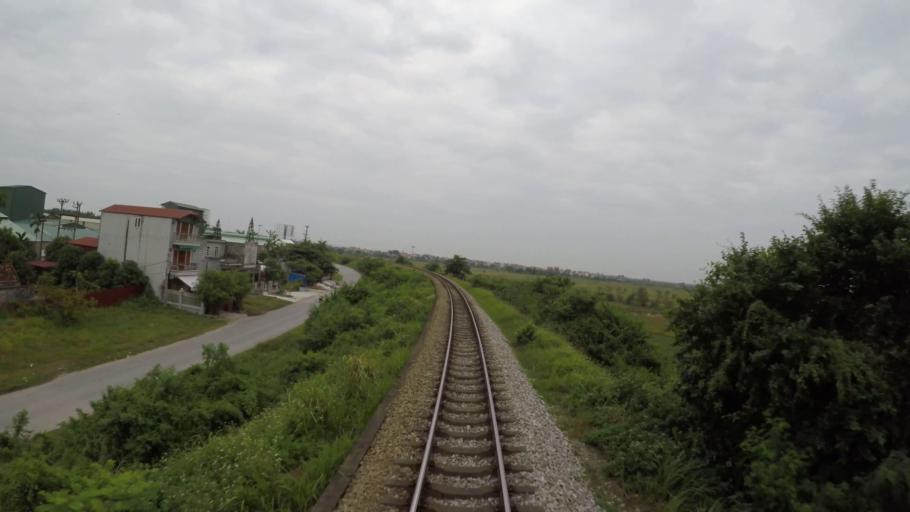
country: VN
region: Hai Duong
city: Thanh Pho Hai Duong
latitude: 20.9582
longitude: 106.3676
